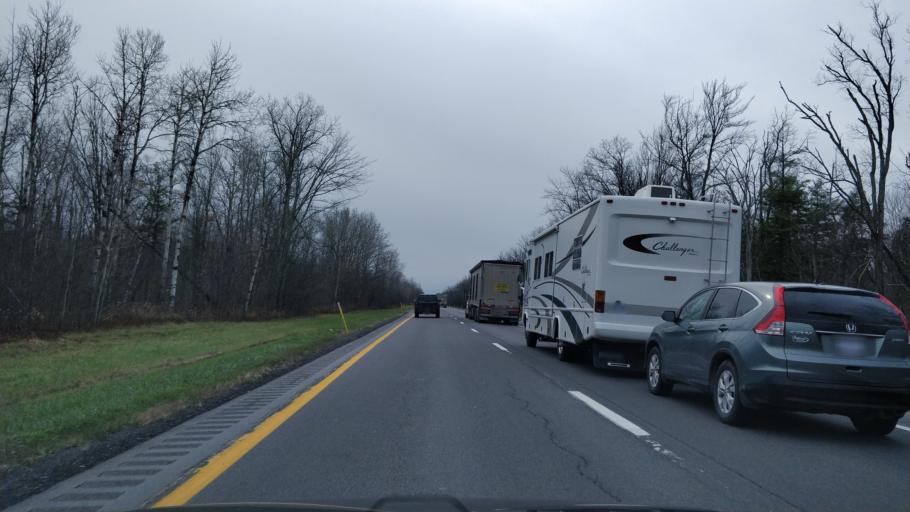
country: US
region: New York
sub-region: Jefferson County
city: Adams
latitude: 43.7700
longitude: -76.0491
